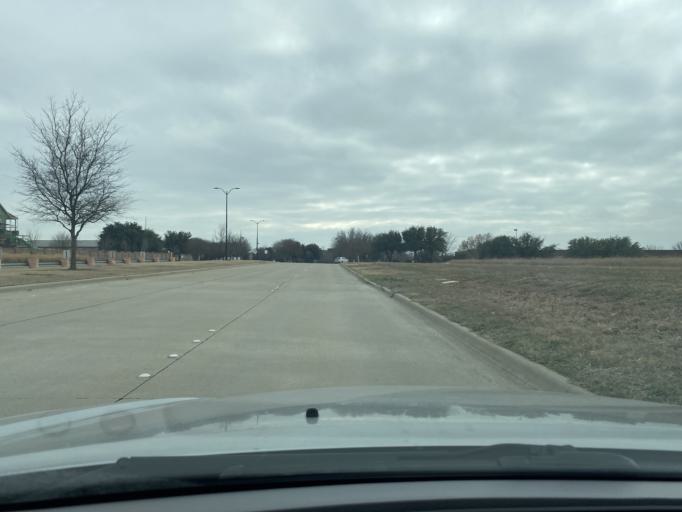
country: US
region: Texas
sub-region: Collin County
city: Frisco
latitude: 33.1128
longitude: -96.8160
